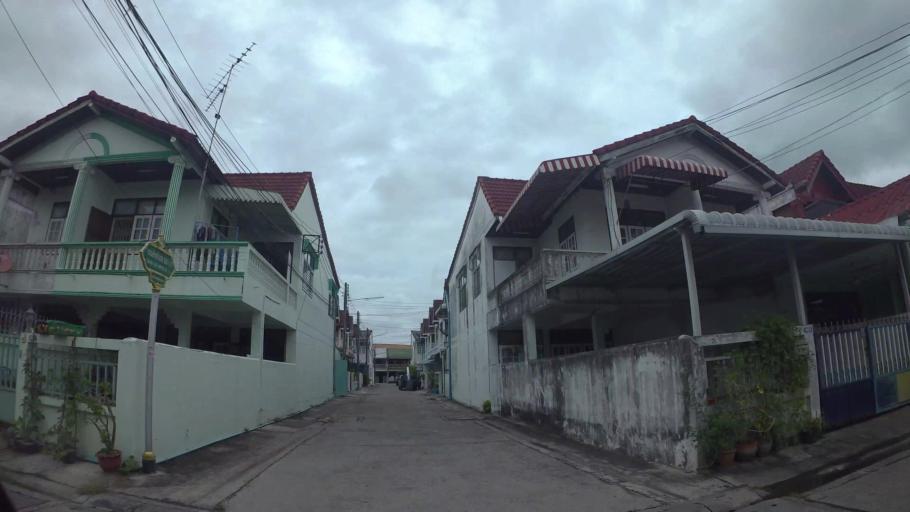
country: TH
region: Rayong
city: Rayong
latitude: 12.6698
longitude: 101.2760
